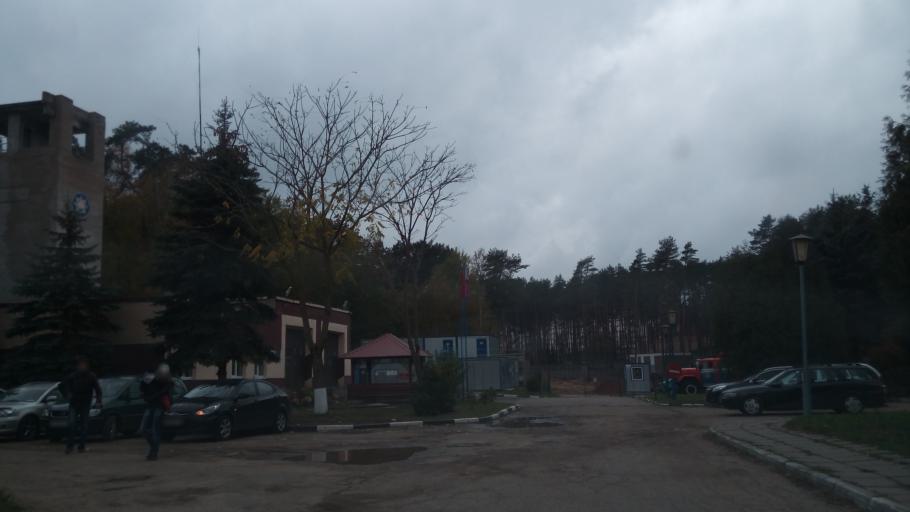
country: BY
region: Minsk
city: Zhdanovichy
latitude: 53.9615
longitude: 27.4425
